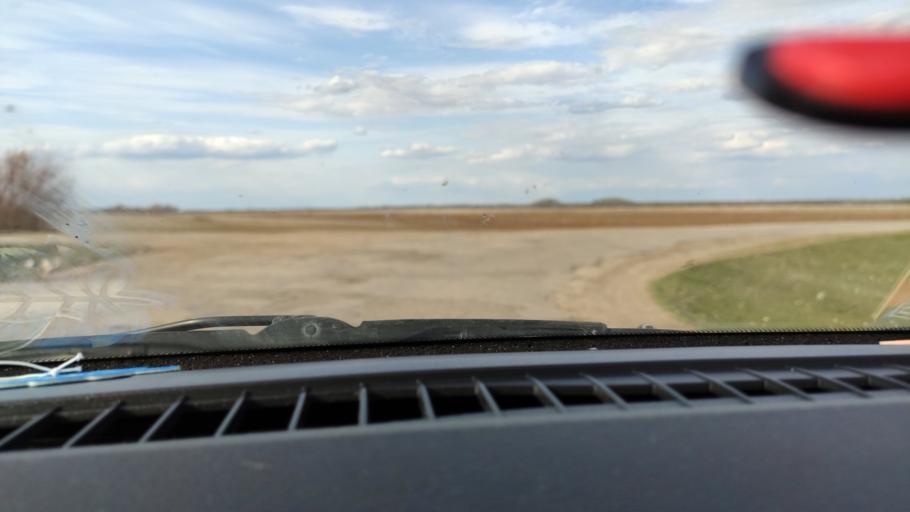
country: RU
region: Saratov
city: Rovnoye
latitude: 50.9382
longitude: 46.0992
